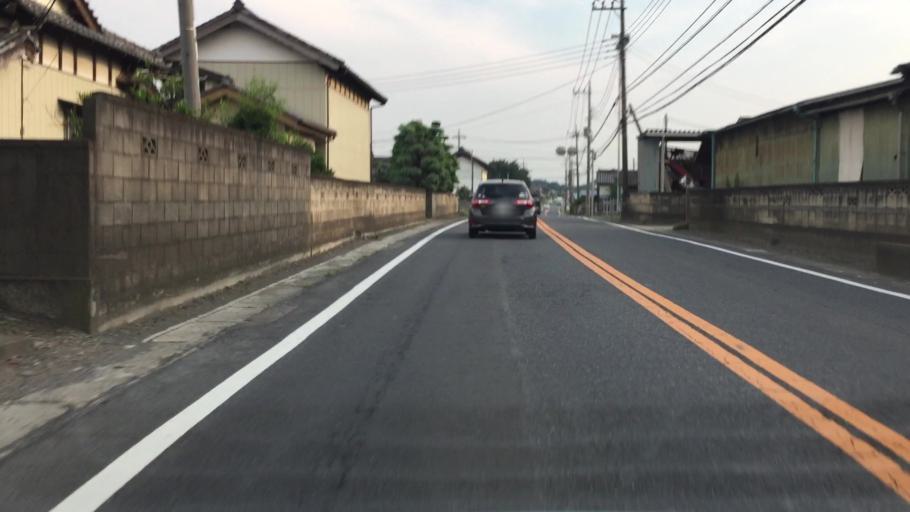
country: JP
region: Tochigi
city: Fujioka
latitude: 36.2856
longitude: 139.6658
